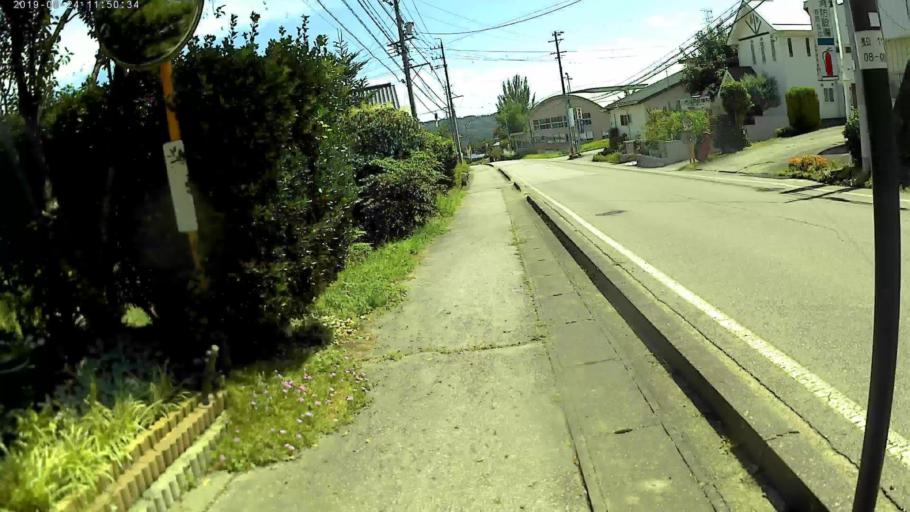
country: JP
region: Nagano
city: Kamimaruko
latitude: 36.2713
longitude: 138.3482
